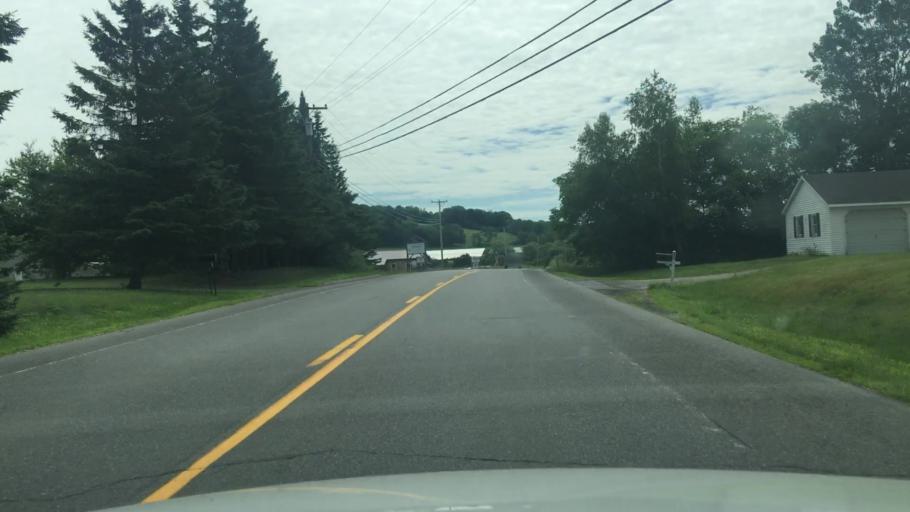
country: US
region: Maine
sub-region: Waldo County
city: Troy
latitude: 44.6093
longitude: -69.3072
